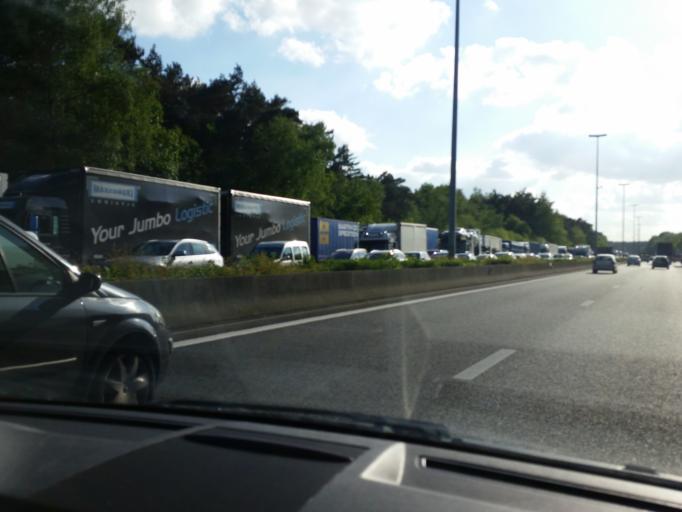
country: BE
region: Flanders
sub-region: Provincie Oost-Vlaanderen
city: Waasmunster
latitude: 51.1299
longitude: 4.0980
